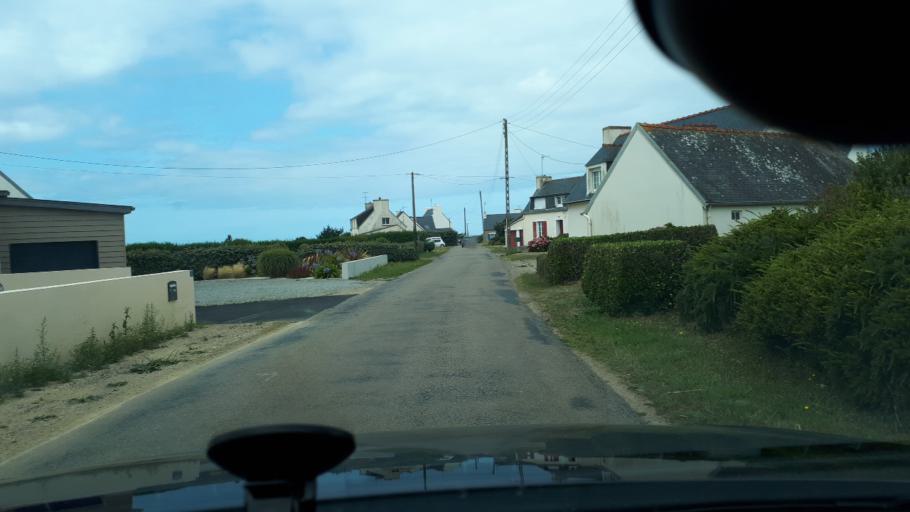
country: FR
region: Brittany
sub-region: Departement du Finistere
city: Pouldreuzic
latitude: 47.9587
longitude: -4.3949
